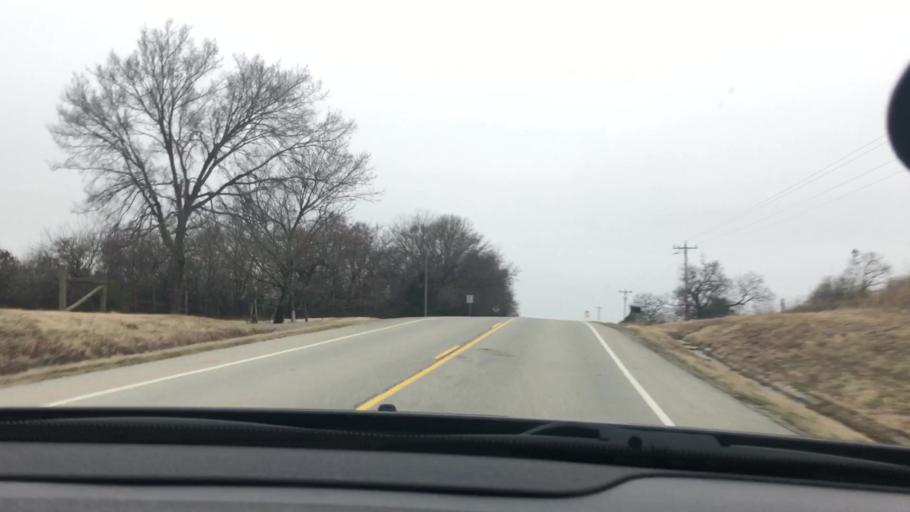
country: US
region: Oklahoma
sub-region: Coal County
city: Coalgate
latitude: 34.5055
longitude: -96.3675
